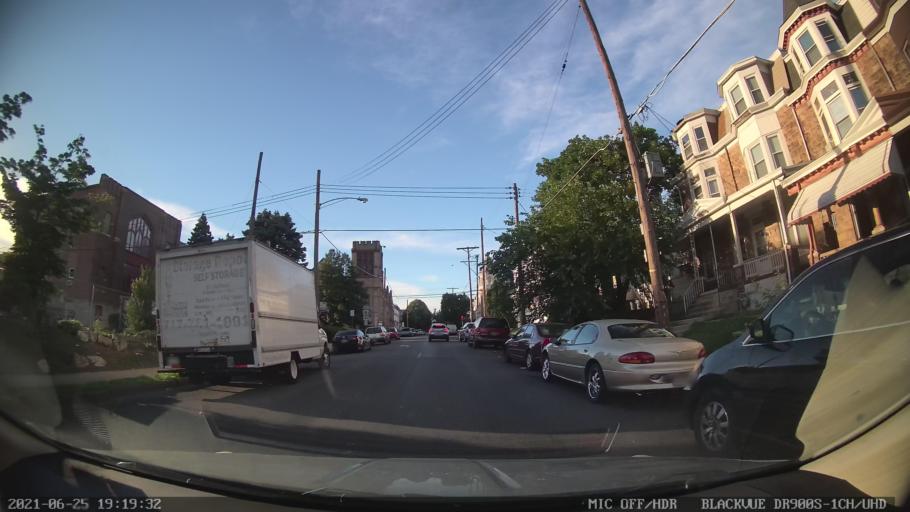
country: US
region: Pennsylvania
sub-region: Berks County
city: Reading
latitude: 40.3484
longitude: -75.9353
